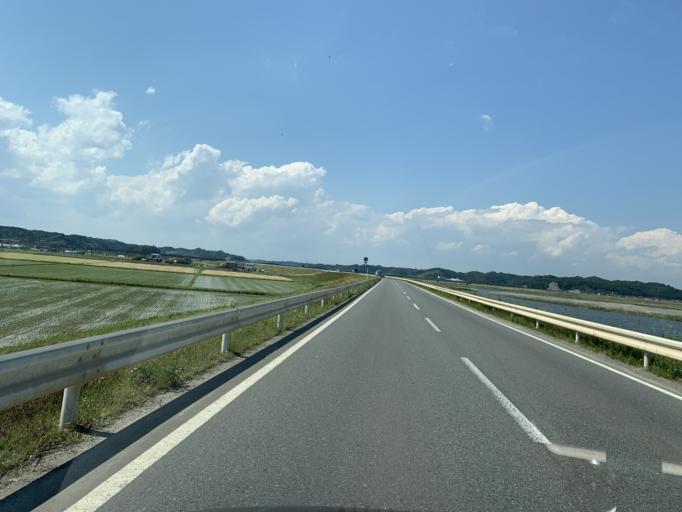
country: JP
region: Miyagi
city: Yamoto
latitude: 38.3816
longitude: 141.1686
